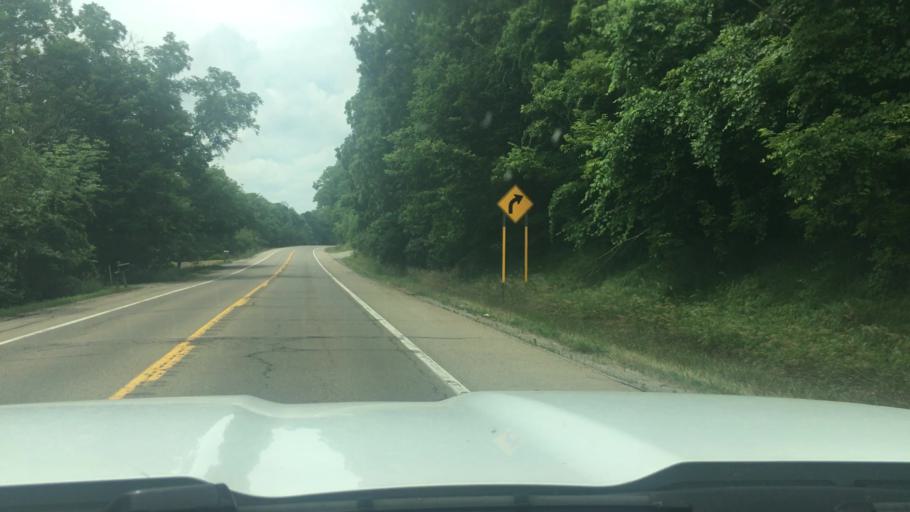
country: US
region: Michigan
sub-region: Kent County
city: Lowell
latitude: 42.9254
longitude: -85.4068
